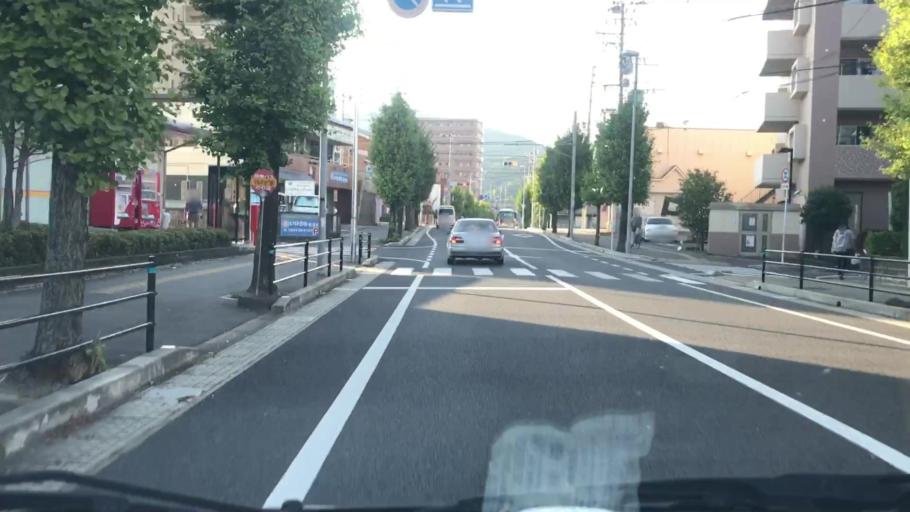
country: JP
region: Saga Prefecture
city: Takeocho-takeo
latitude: 33.1926
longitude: 130.0235
